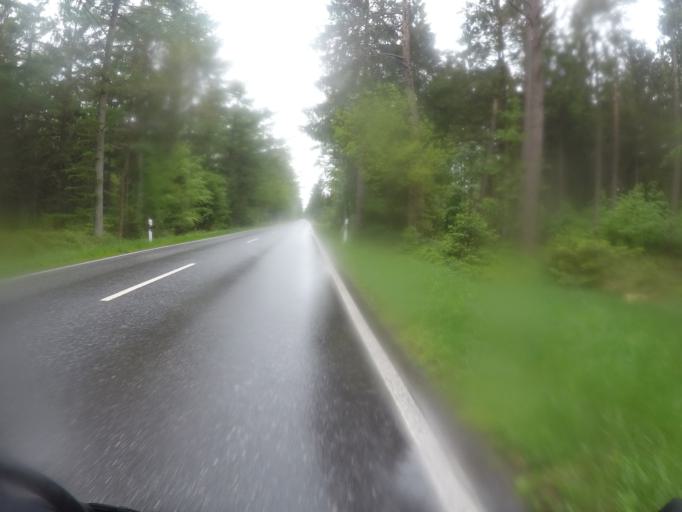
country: DE
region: Schleswig-Holstein
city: Heidmuhlen
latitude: 53.9386
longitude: 10.0884
